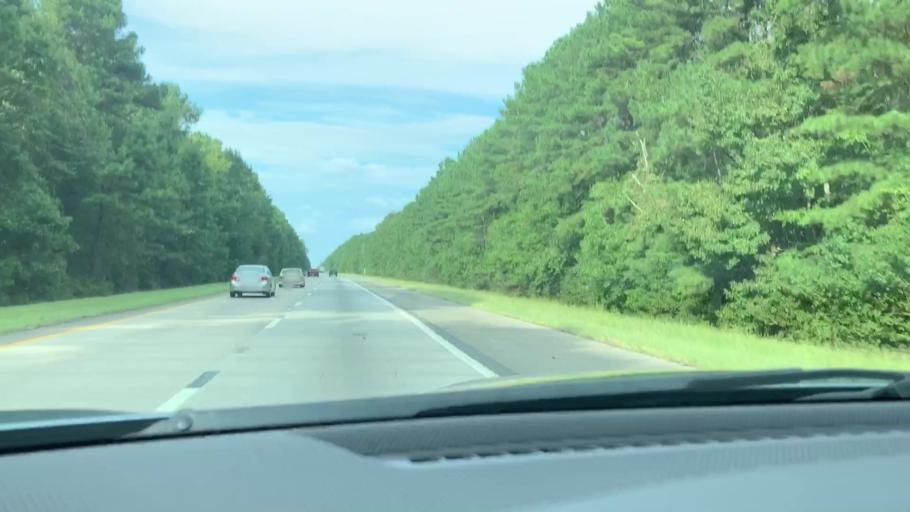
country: US
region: South Carolina
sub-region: Colleton County
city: Walterboro
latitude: 32.9653
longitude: -80.6771
